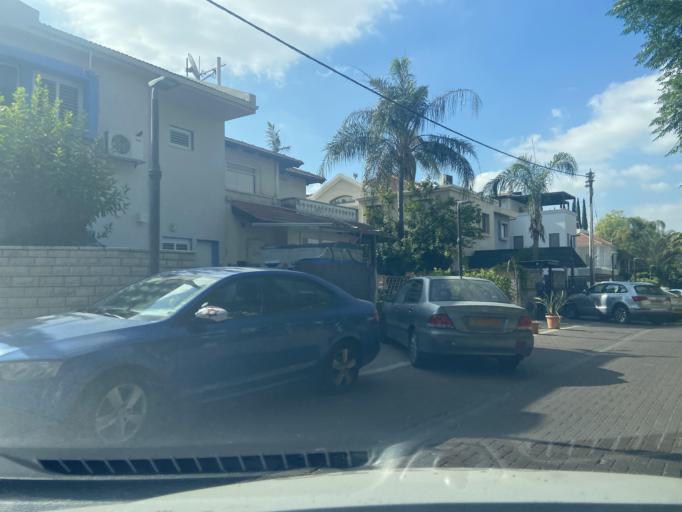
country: IL
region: Central District
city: Yehud
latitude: 32.0343
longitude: 34.8937
